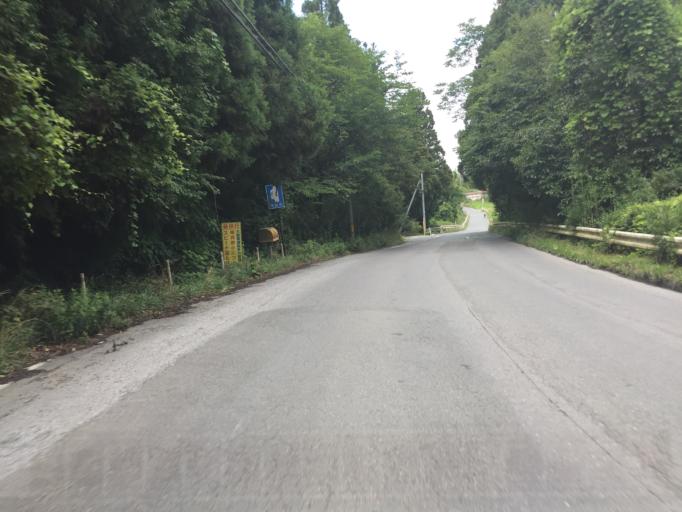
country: JP
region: Miyagi
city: Marumori
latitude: 37.7622
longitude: 140.9158
